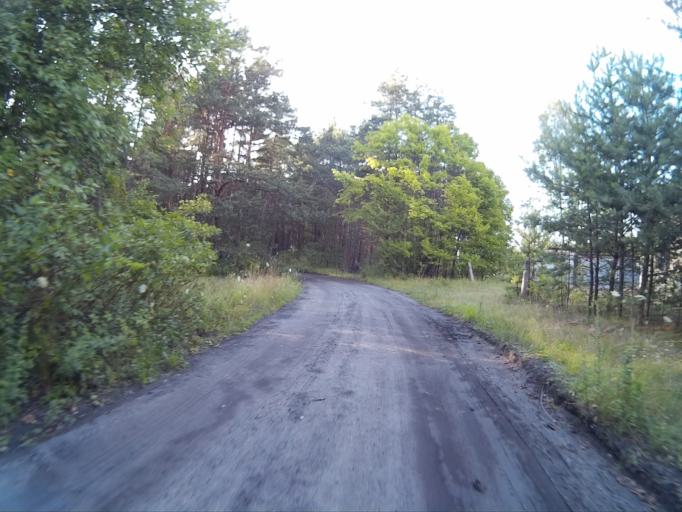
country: PL
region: Kujawsko-Pomorskie
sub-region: Powiat swiecki
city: Lniano
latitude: 53.5466
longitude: 18.1116
